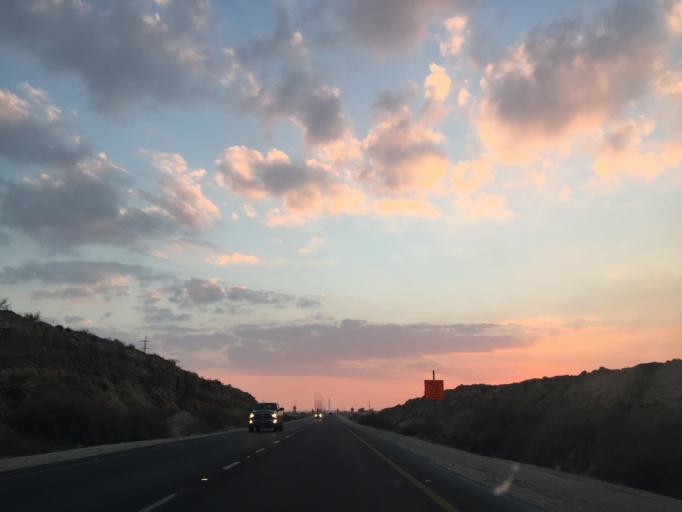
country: IL
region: Southern District
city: Yeroham
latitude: 31.0288
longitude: 34.7992
